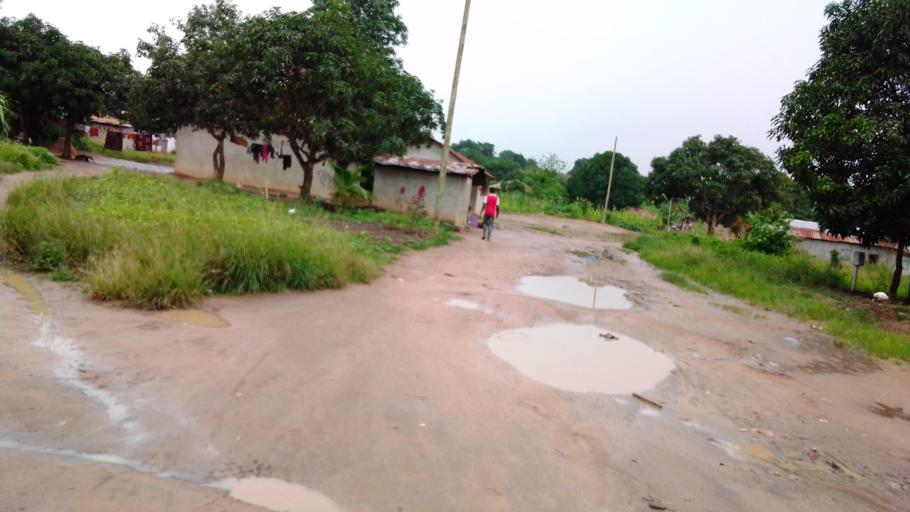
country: SL
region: Eastern Province
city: Kenema
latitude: 7.8621
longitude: -11.1721
